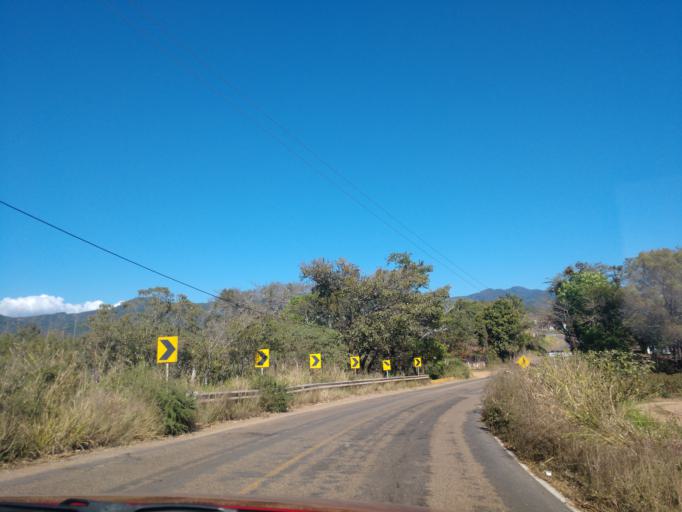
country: MX
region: Nayarit
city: Compostela
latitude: 21.2715
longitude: -104.8904
